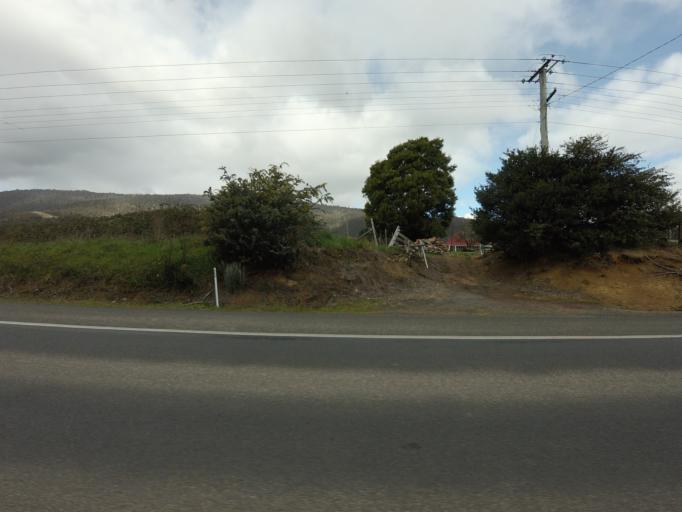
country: AU
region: Tasmania
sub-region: Huon Valley
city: Huonville
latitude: -43.0456
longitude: 147.0423
